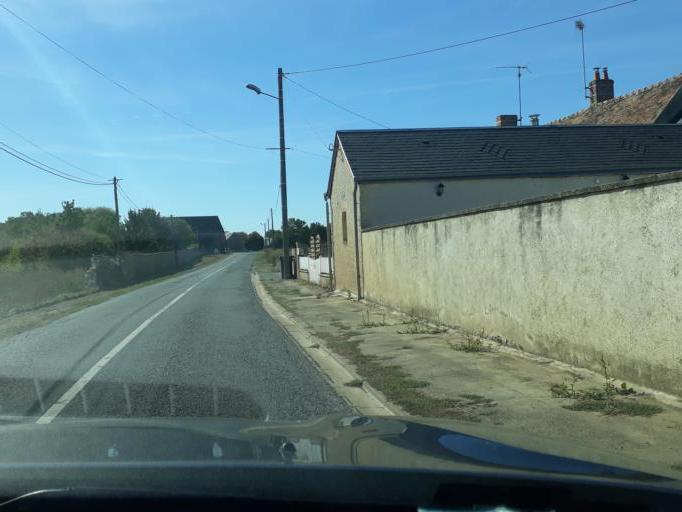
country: FR
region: Centre
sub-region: Departement du Loir-et-Cher
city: Ouzouer-le-Marche
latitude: 47.9450
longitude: 1.5259
